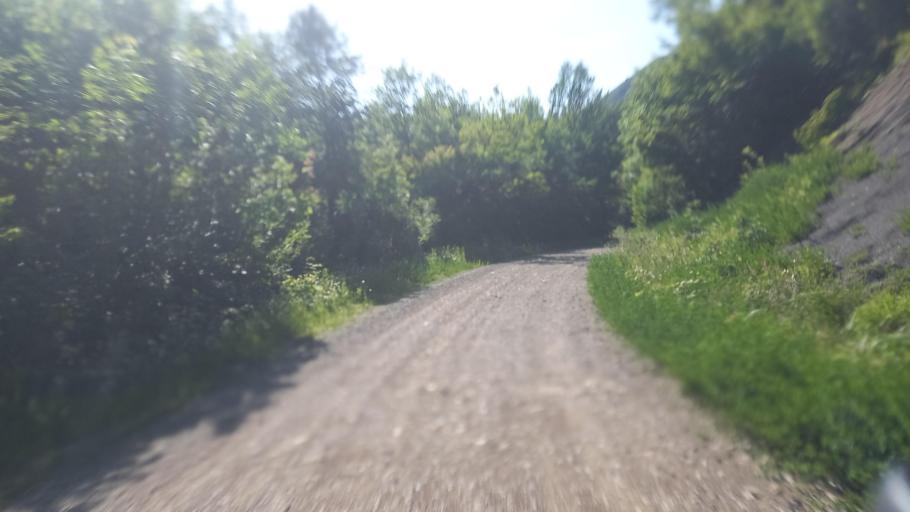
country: RU
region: Krasnodarskiy
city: Dzhubga
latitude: 44.5377
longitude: 38.7811
